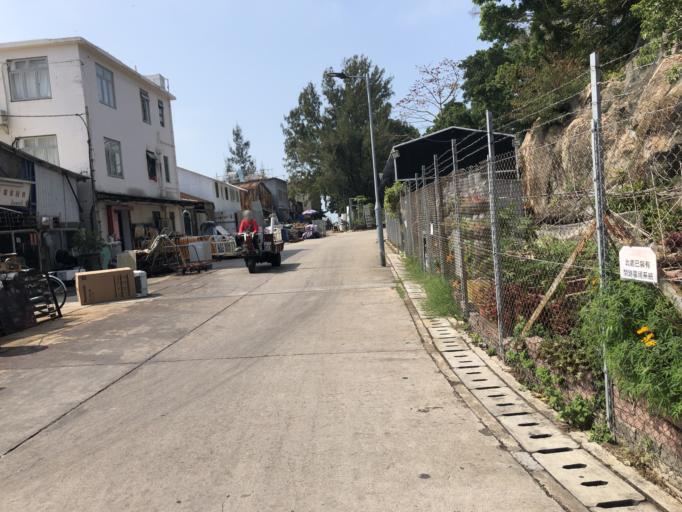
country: HK
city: Yung Shue Wan
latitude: 22.2120
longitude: 114.0249
